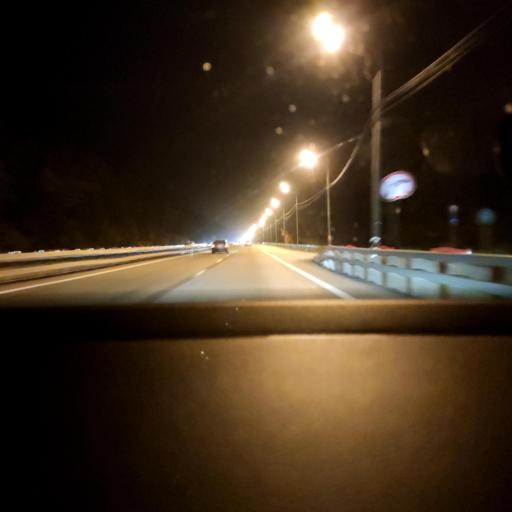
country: RU
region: Moskovskaya
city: Selyatino
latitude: 55.5041
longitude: 36.9770
